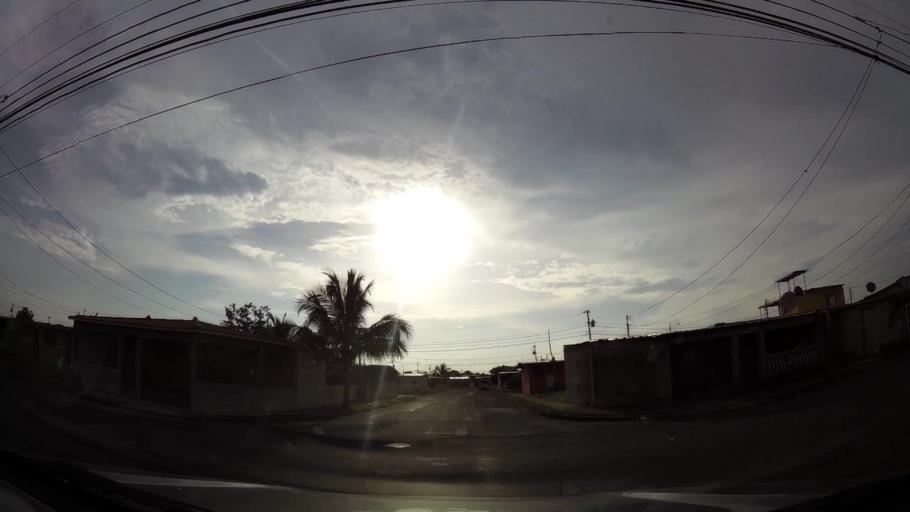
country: PA
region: Panama
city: Tocumen
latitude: 9.0794
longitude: -79.3548
